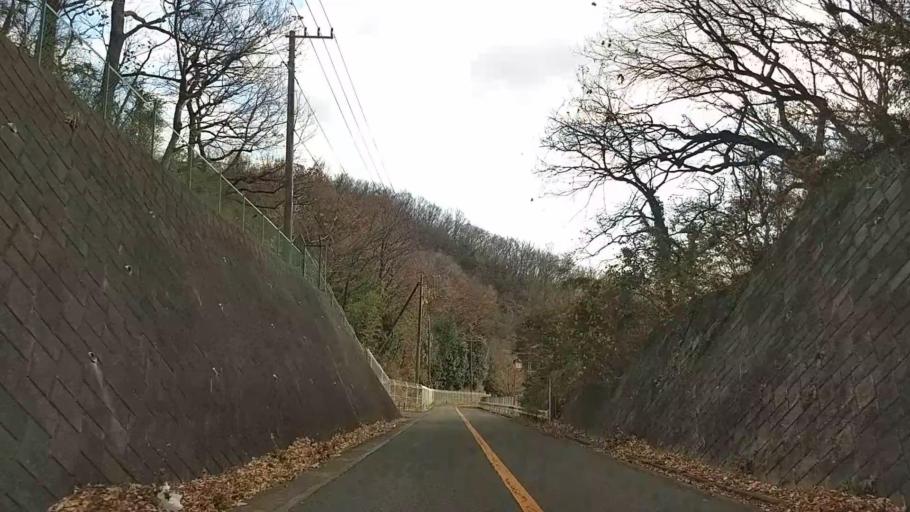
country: JP
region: Kanagawa
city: Isehara
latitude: 35.4232
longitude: 139.3135
